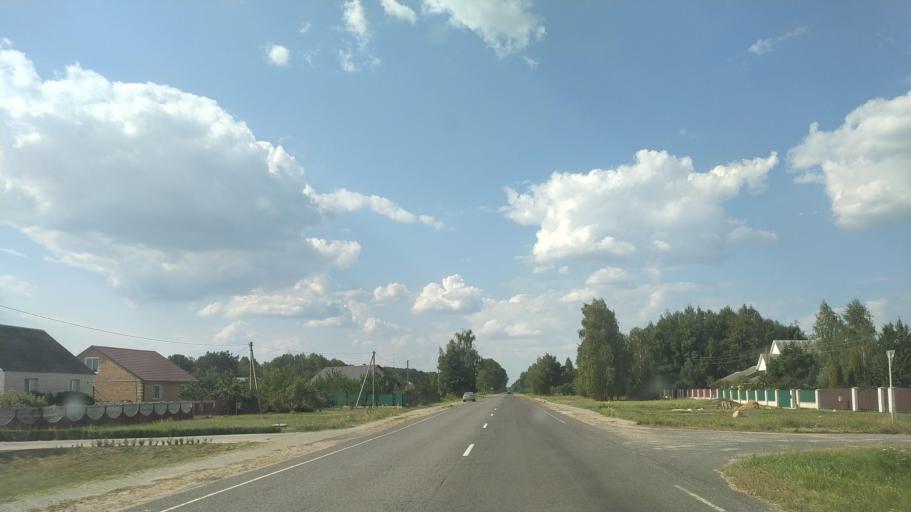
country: BY
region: Brest
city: Drahichyn
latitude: 52.2058
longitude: 25.1431
